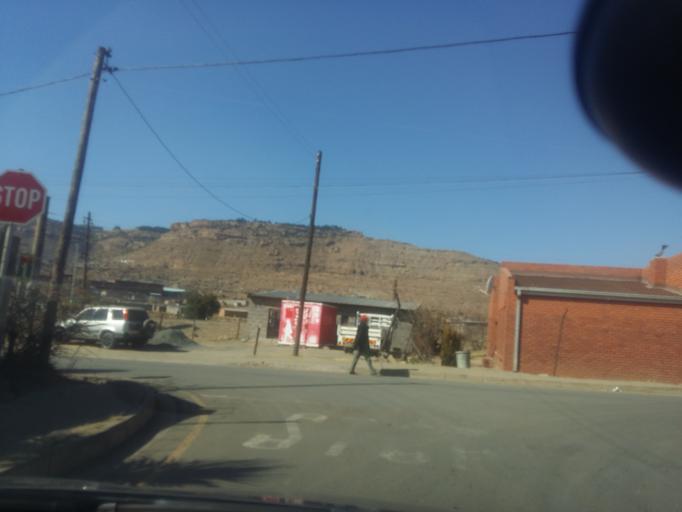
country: LS
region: Maseru
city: Maseru
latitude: -29.3444
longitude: 27.4567
